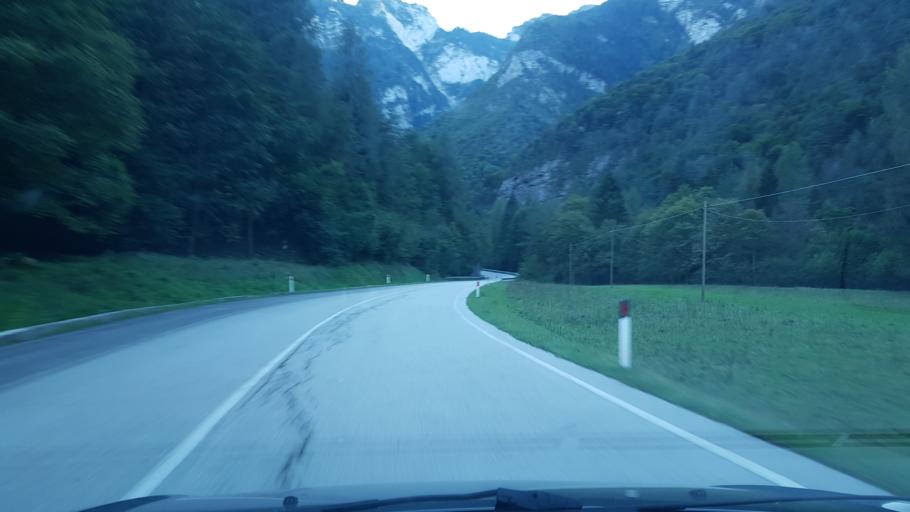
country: IT
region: Veneto
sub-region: Provincia di Belluno
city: Forno di Zoldo
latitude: 46.3165
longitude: 12.2298
